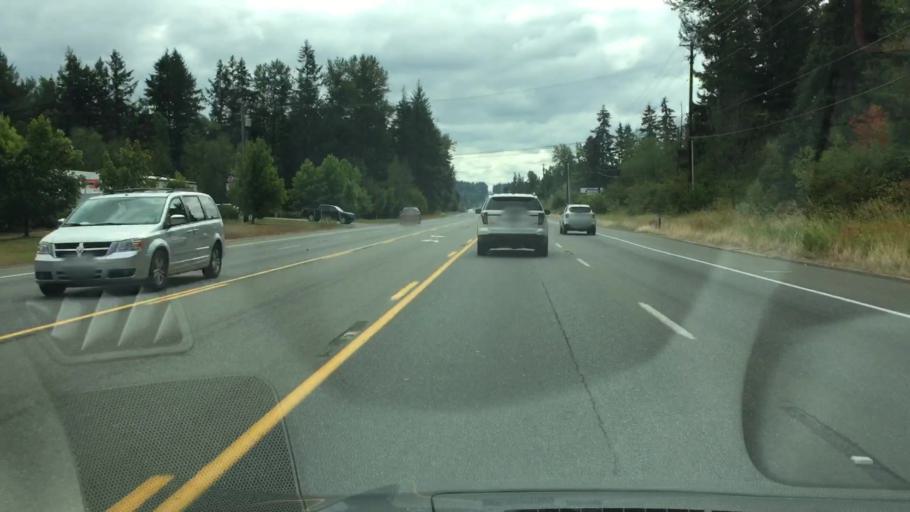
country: US
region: Washington
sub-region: Pierce County
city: Graham
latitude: 47.0692
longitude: -122.2946
